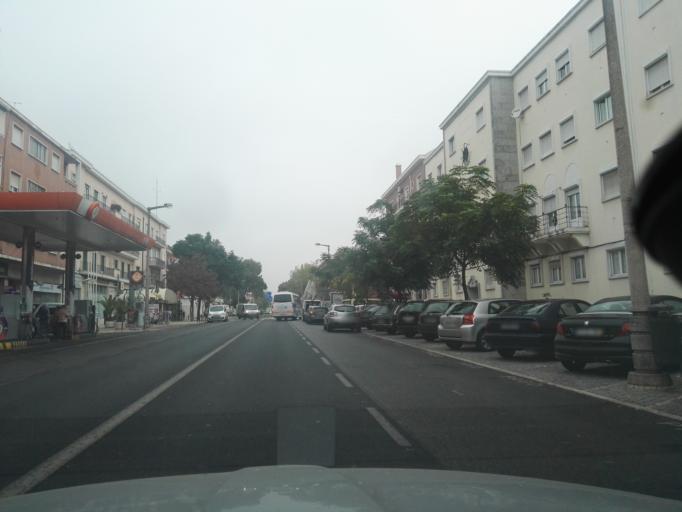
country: PT
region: Lisbon
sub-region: Lisbon
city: Lisbon
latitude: 38.7539
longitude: -9.1385
